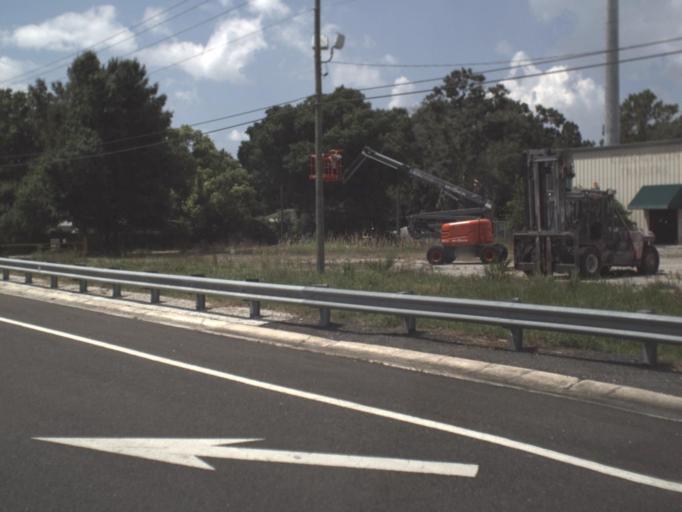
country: US
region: Florida
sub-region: Hillsborough County
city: East Lake-Orient Park
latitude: 27.9697
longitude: -82.3605
